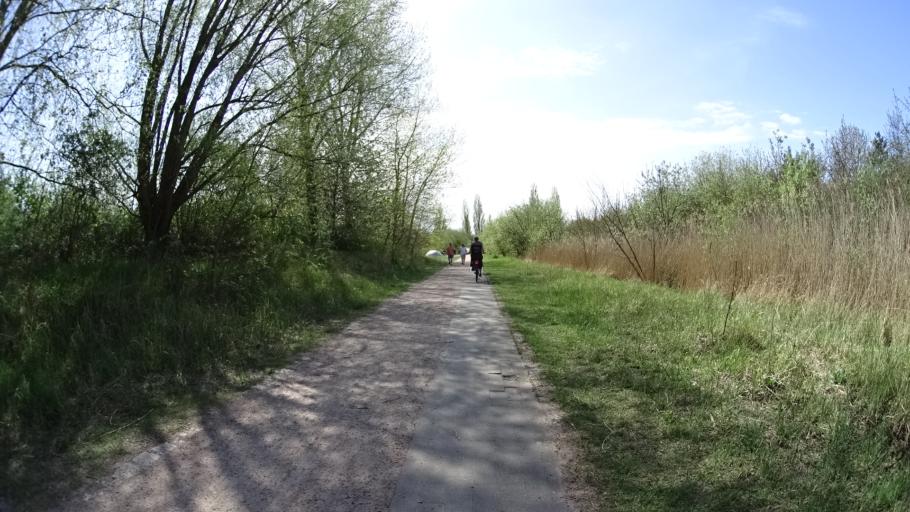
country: DE
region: Hamburg
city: Altona
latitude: 53.5407
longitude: 9.8586
